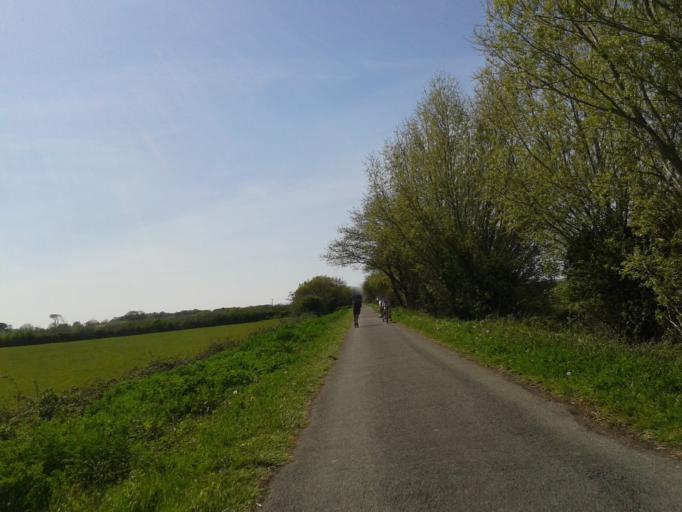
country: GB
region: England
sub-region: Devon
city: Fremington
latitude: 51.0743
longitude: -4.1446
